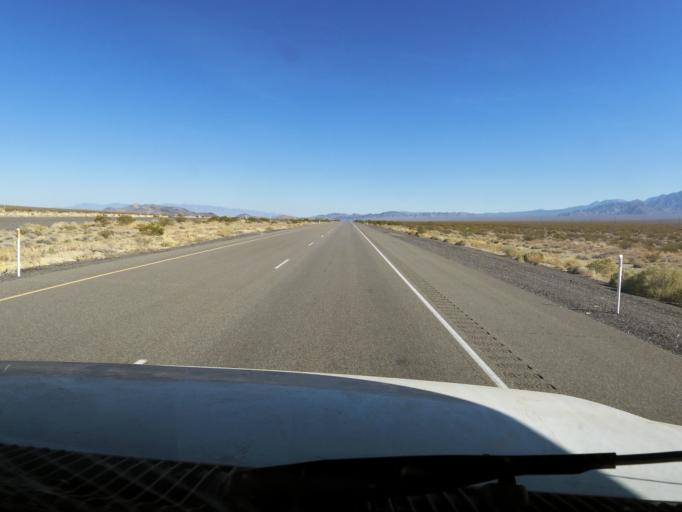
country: US
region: Nevada
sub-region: Nye County
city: Pahrump
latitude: 36.5974
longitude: -115.9547
